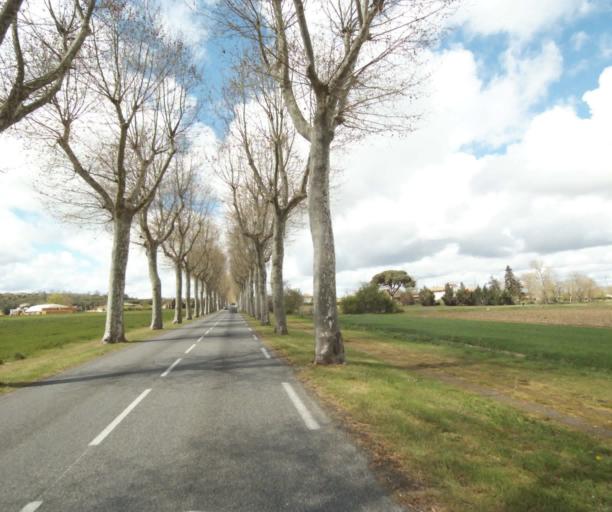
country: FR
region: Midi-Pyrenees
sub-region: Departement de l'Ariege
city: Saverdun
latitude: 43.2317
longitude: 1.5896
